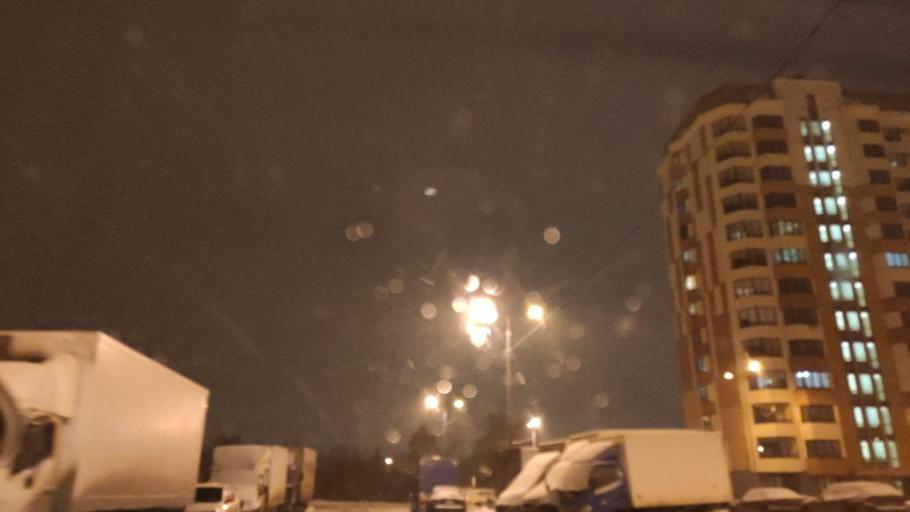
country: RU
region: Moskovskaya
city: Shcherbinka
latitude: 55.5438
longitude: 37.5656
